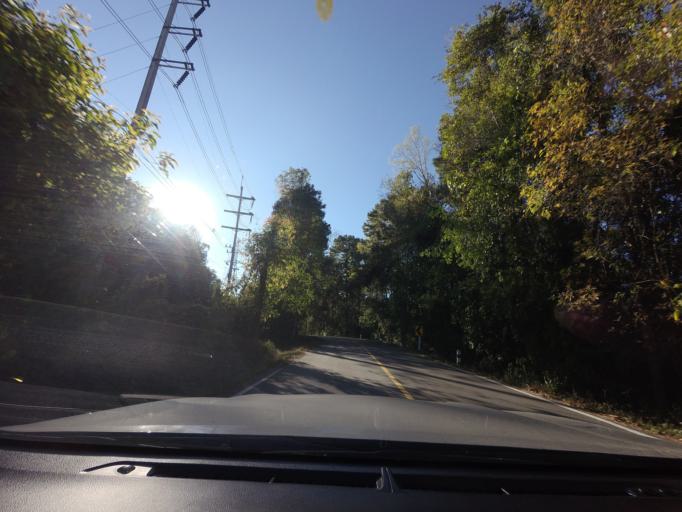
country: TH
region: Mae Hong Son
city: Mae Hi
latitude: 19.2793
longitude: 98.6146
